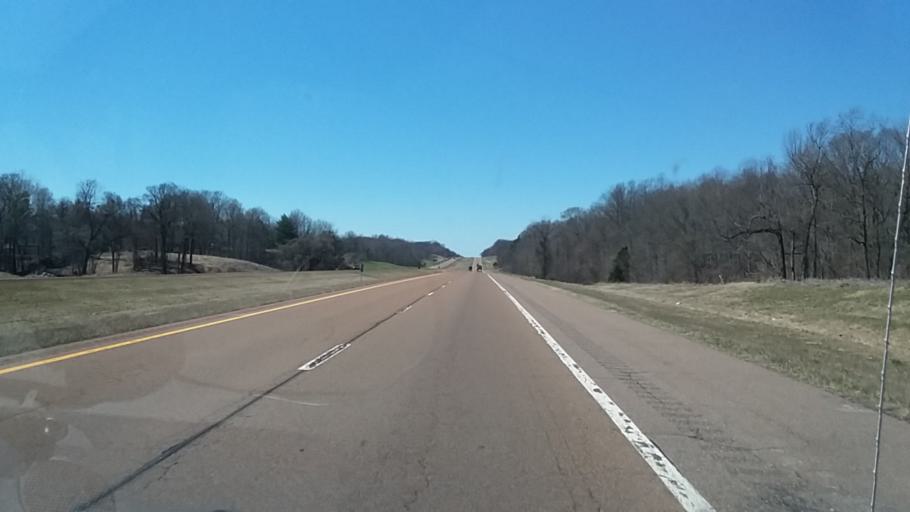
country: US
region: Tennessee
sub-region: Dyer County
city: Dyersburg
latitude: 36.0720
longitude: -89.4652
